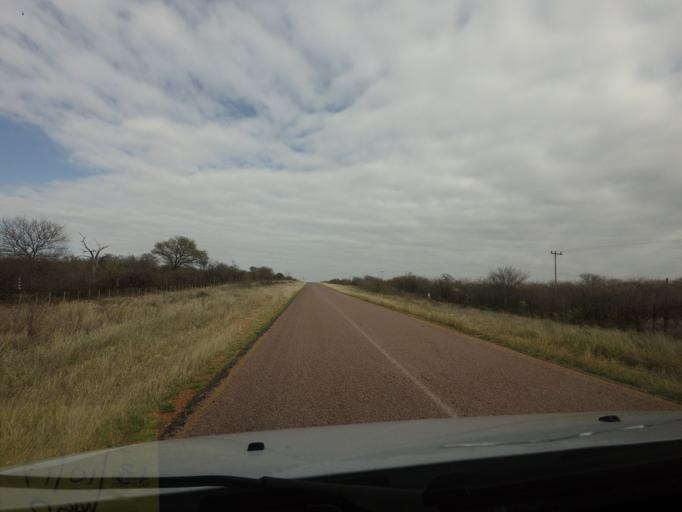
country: ZA
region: Limpopo
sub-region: Vhembe District Municipality
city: Messina
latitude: -22.6429
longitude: 29.9291
